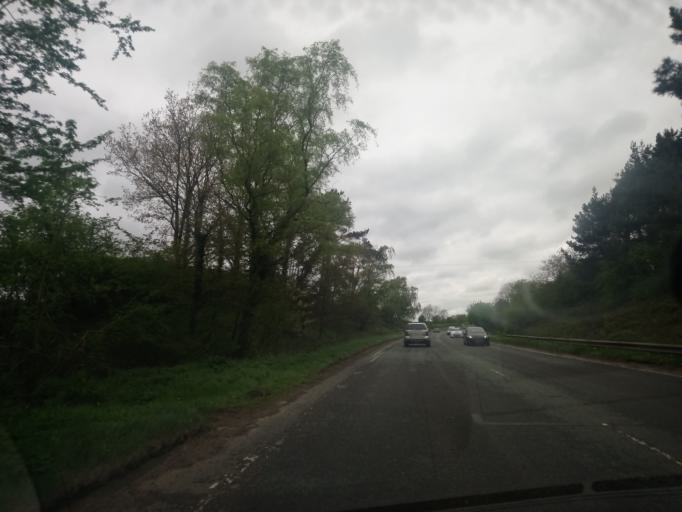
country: GB
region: England
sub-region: Telford and Wrekin
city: Chetwynd
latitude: 52.8108
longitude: -2.4407
